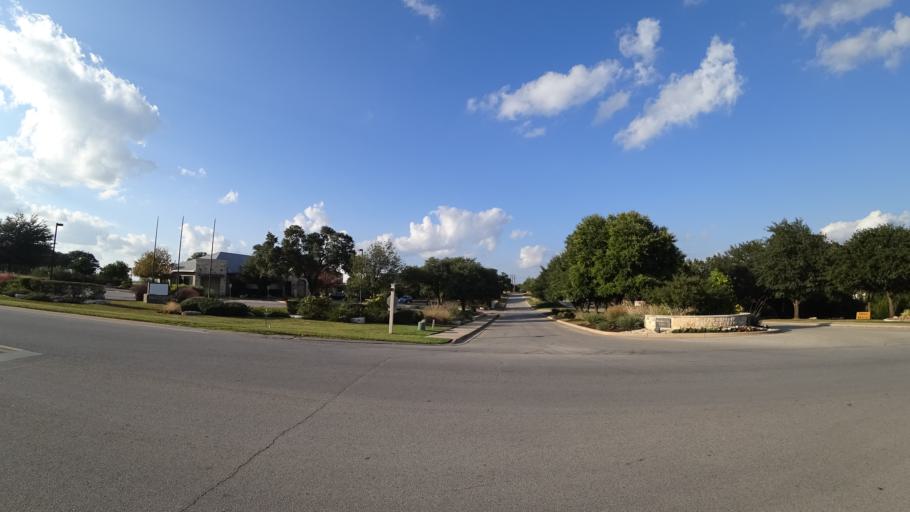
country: US
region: Texas
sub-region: Travis County
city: Barton Creek
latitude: 30.2887
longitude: -97.8726
